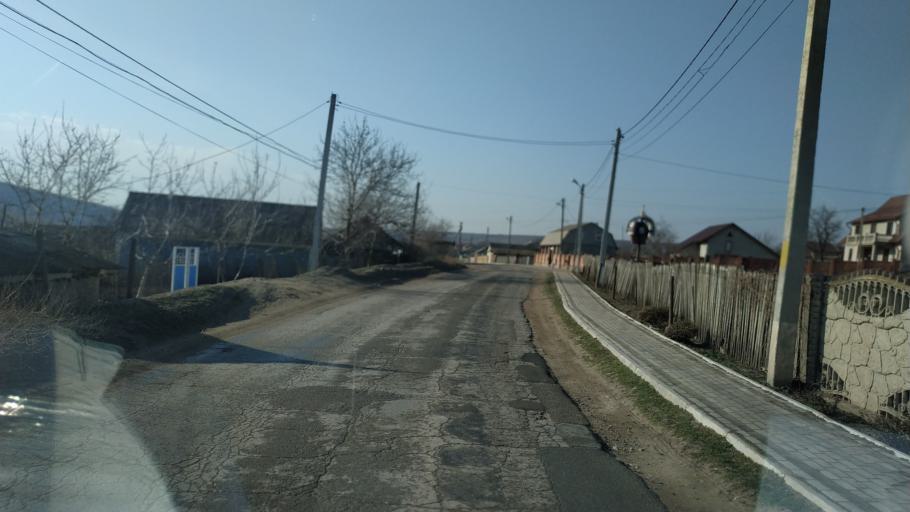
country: MD
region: Chisinau
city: Singera
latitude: 46.8102
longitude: 29.0367
